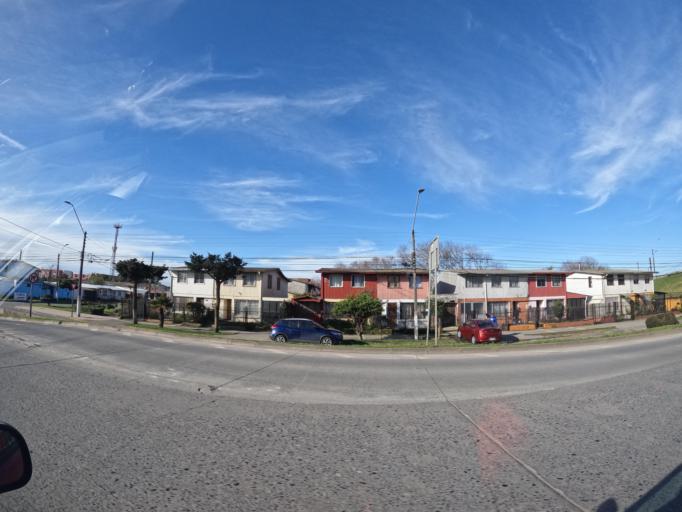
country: CL
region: Biobio
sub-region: Provincia de Concepcion
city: Talcahuano
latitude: -36.7651
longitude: -73.0862
